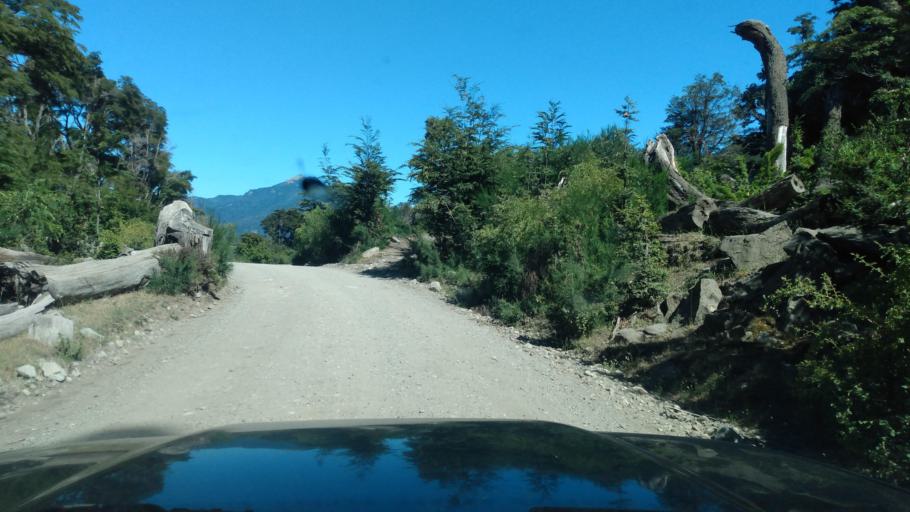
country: AR
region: Neuquen
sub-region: Departamento de Lacar
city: San Martin de los Andes
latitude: -39.7523
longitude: -71.4546
